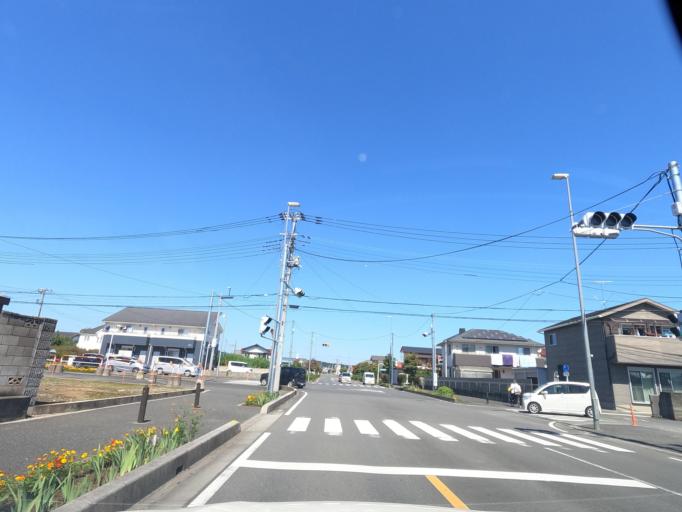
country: JP
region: Saitama
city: Hanno
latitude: 35.8522
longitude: 139.3375
